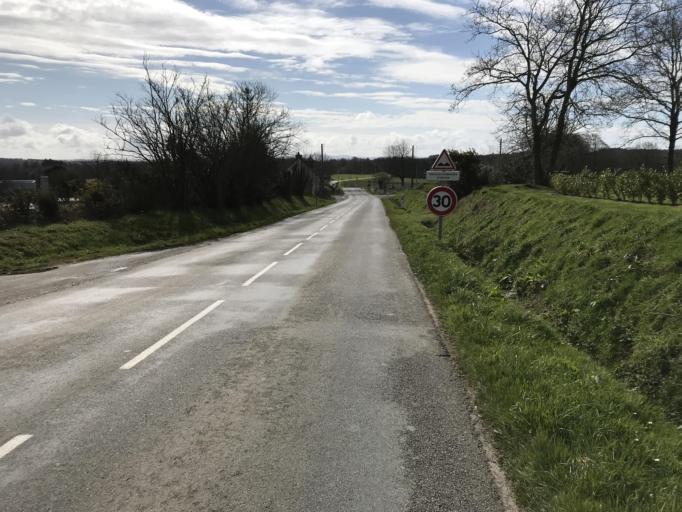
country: FR
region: Brittany
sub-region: Departement du Finistere
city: Dirinon
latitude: 48.3896
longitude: -4.2667
